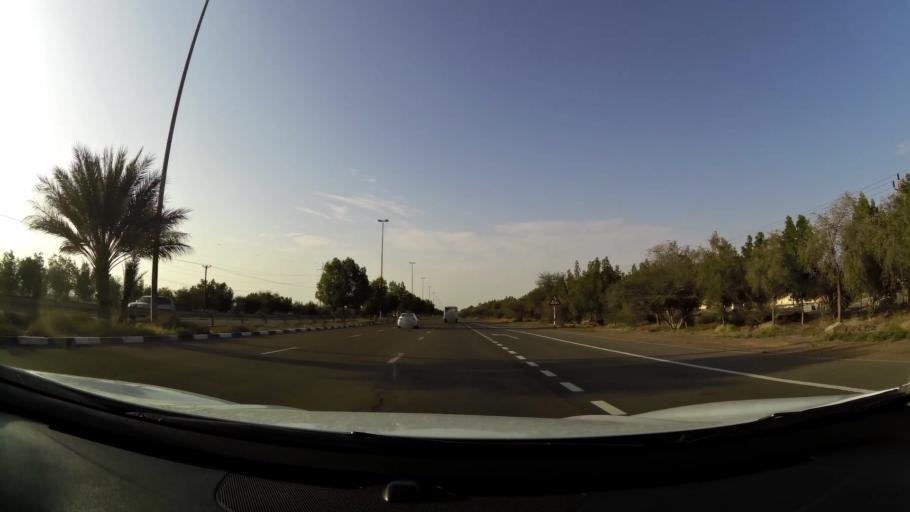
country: AE
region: Abu Dhabi
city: Al Ain
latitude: 24.1343
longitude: 55.8179
